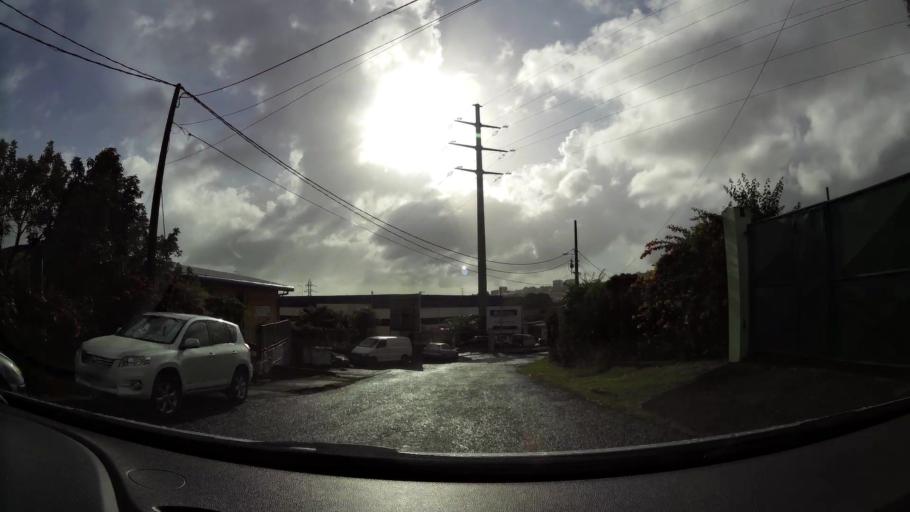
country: MQ
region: Martinique
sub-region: Martinique
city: Fort-de-France
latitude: 14.6166
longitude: -61.0446
